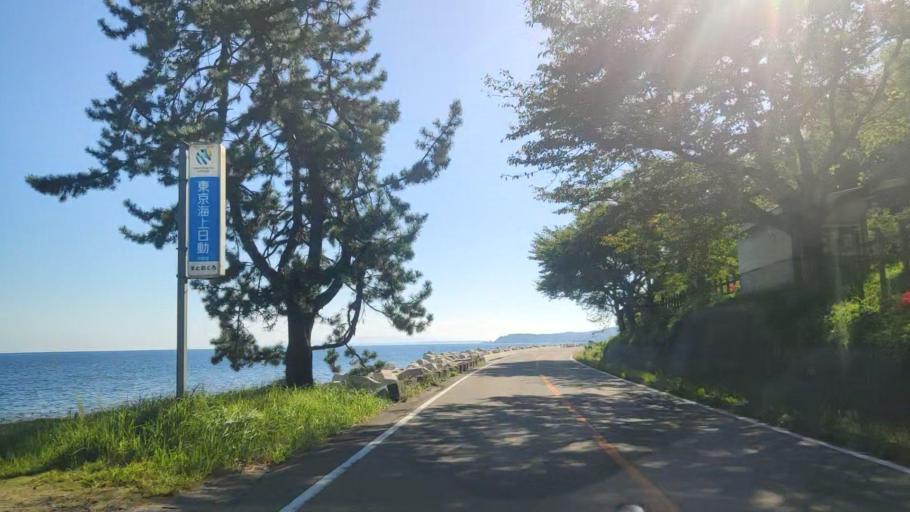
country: JP
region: Ishikawa
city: Nanao
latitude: 37.2874
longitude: 137.1153
